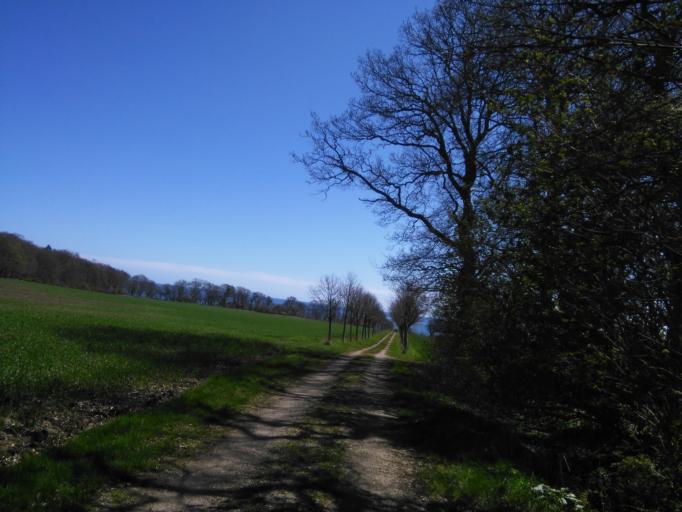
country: DK
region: Central Jutland
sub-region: Hedensted Kommune
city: Juelsminde
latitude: 55.7433
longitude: 10.0377
